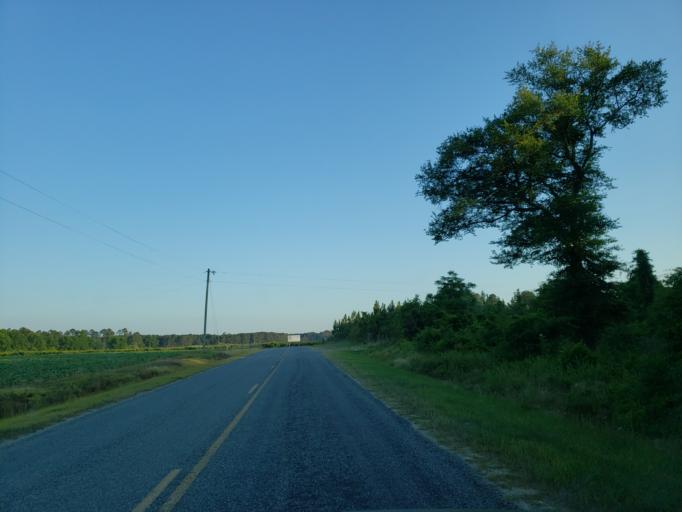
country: US
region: Georgia
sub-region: Dooly County
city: Vienna
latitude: 32.0918
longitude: -83.7565
